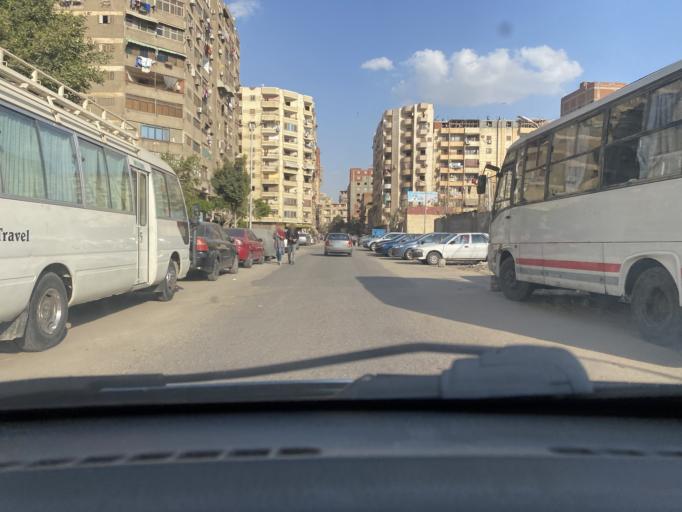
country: EG
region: Muhafazat al Qahirah
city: Cairo
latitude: 30.1067
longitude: 31.3048
